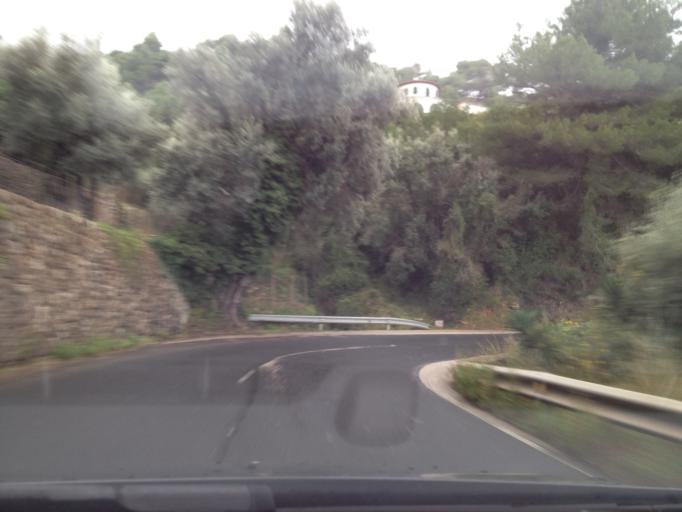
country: ES
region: Balearic Islands
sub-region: Illes Balears
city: Deia
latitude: 39.7583
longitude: 2.6504
